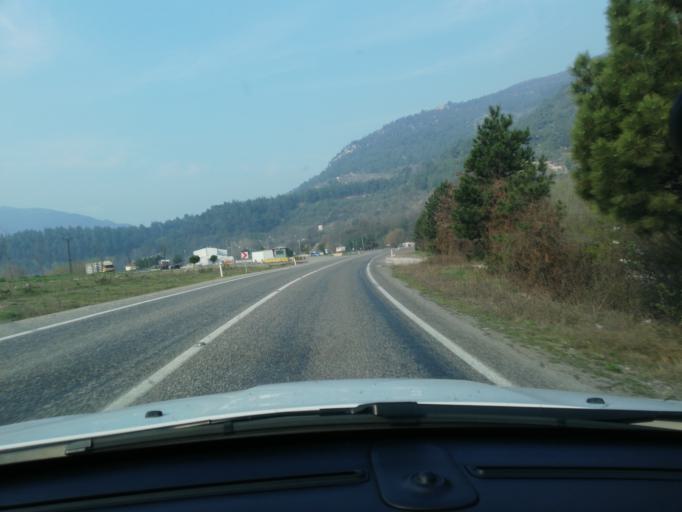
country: TR
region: Karabuk
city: Karabuk
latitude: 41.1730
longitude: 32.5828
